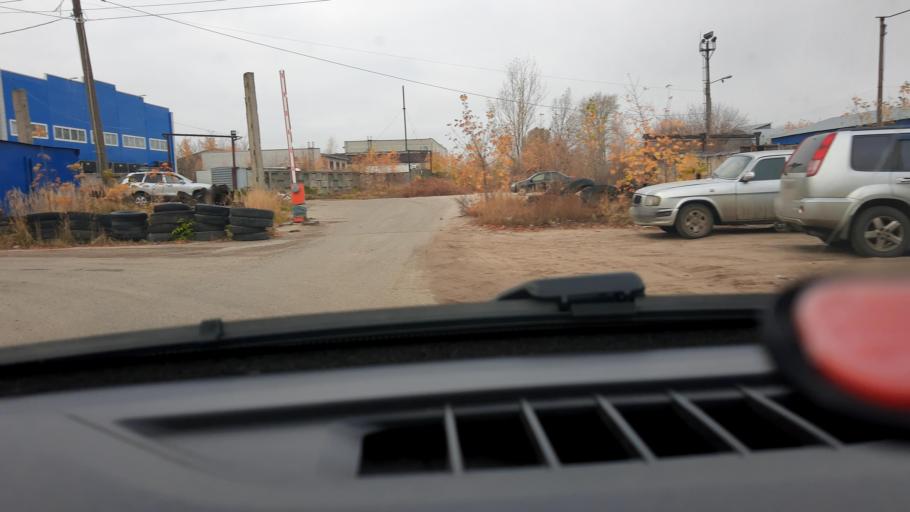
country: RU
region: Nizjnij Novgorod
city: Gorbatovka
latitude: 56.3387
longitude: 43.8149
